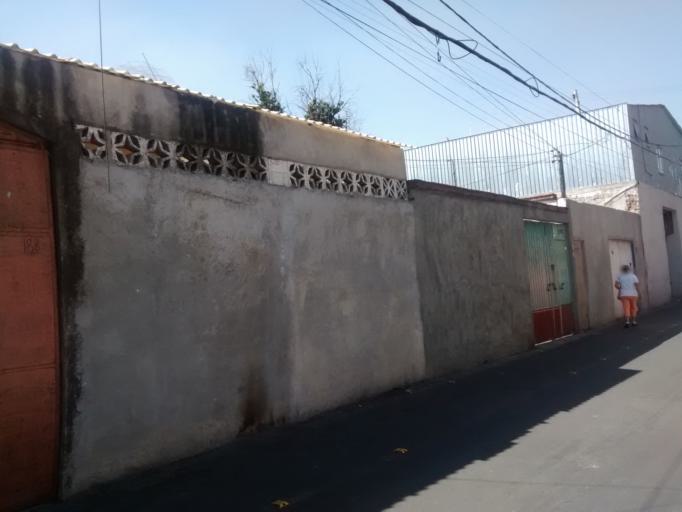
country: MX
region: Mexico City
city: Miguel Hidalgo
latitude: 19.4526
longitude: -99.1965
